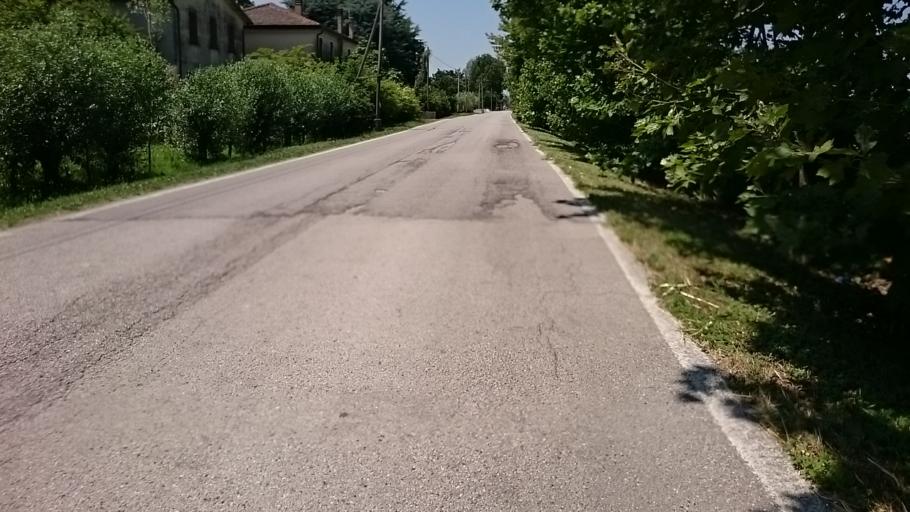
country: IT
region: Veneto
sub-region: Provincia di Venezia
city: Sant'Angelo
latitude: 45.5175
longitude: 12.0008
